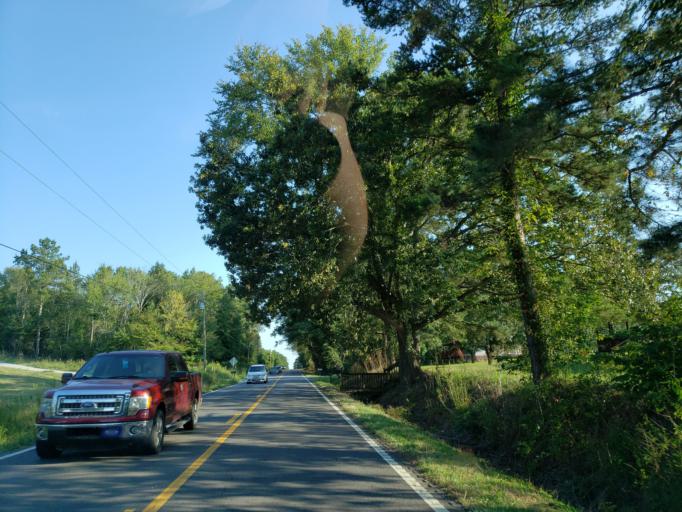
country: US
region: Tennessee
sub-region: Bradley County
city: Wildwood Lake
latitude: 35.0300
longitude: -84.7992
